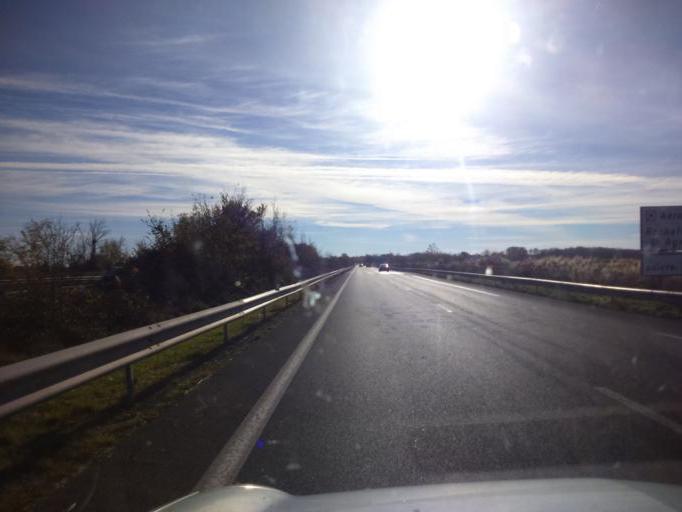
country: FR
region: Poitou-Charentes
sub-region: Departement de la Charente-Maritime
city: Breuil-Magne
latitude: 45.9787
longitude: -0.9968
